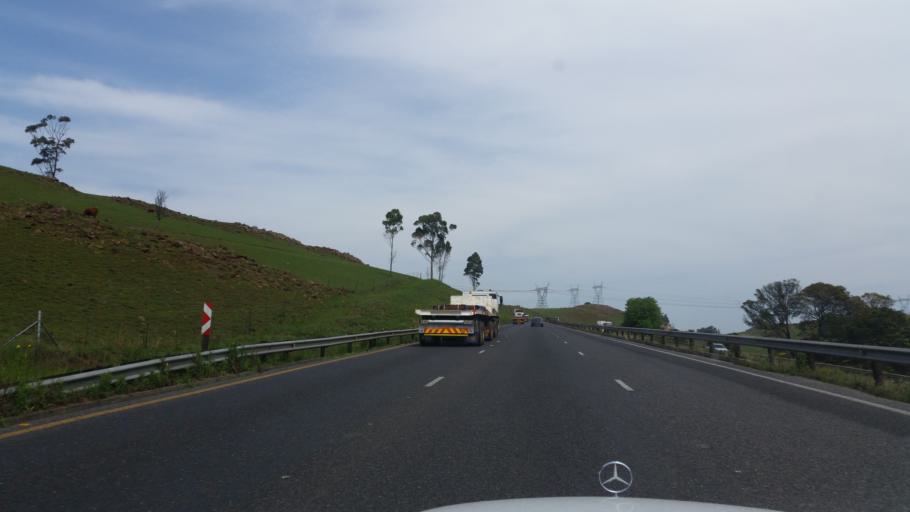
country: ZA
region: KwaZulu-Natal
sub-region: uMgungundlovu District Municipality
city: Howick
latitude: -29.4376
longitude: 30.1727
